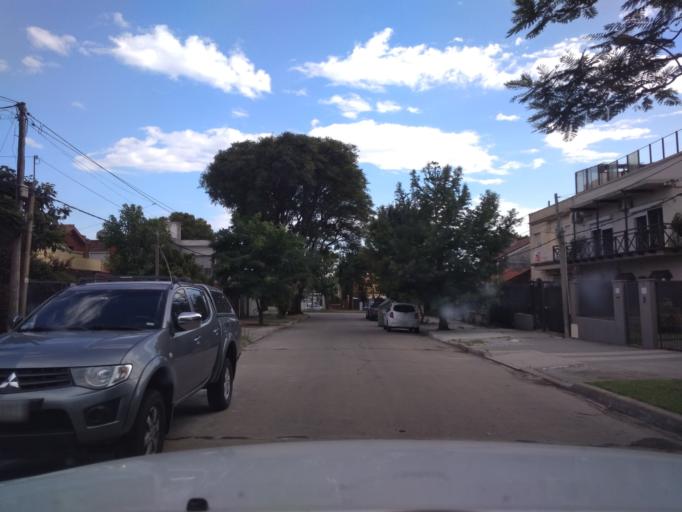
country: UY
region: Canelones
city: Paso de Carrasco
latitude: -34.8932
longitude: -56.0871
